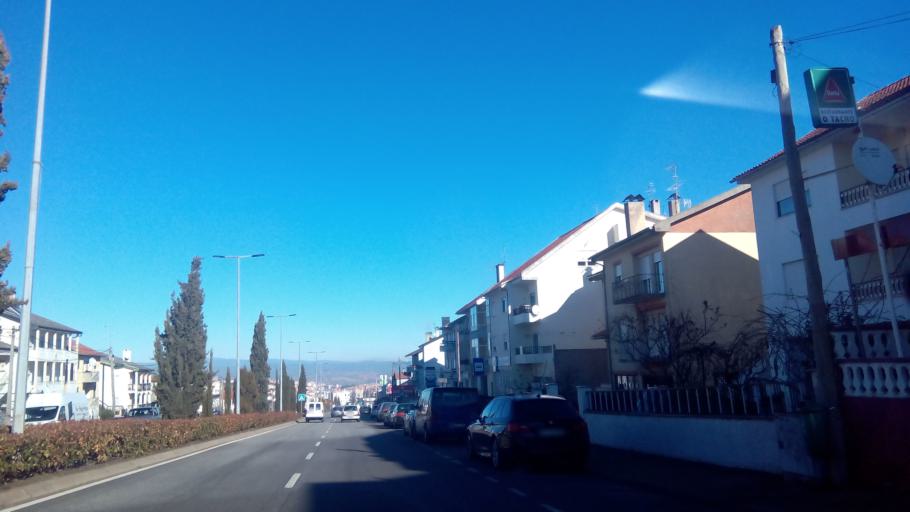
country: PT
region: Braganca
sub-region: Braganca Municipality
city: Braganca
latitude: 41.7826
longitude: -6.7780
